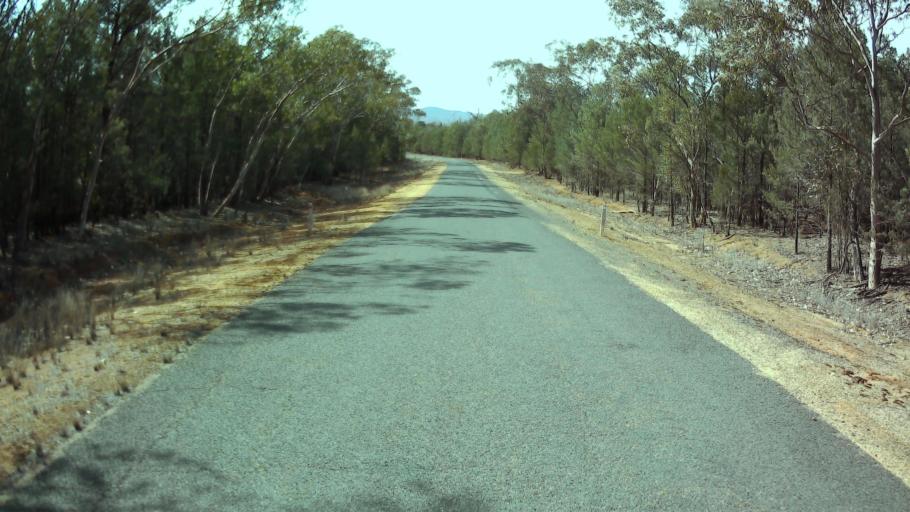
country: AU
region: New South Wales
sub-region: Weddin
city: Grenfell
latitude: -33.7463
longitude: 148.0553
